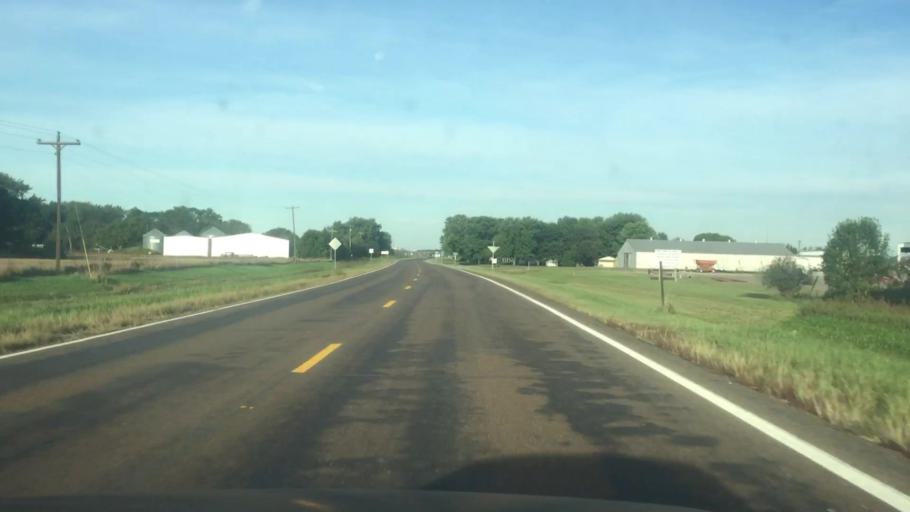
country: US
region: Nebraska
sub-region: Gage County
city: Wymore
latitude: 40.0450
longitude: -96.7981
